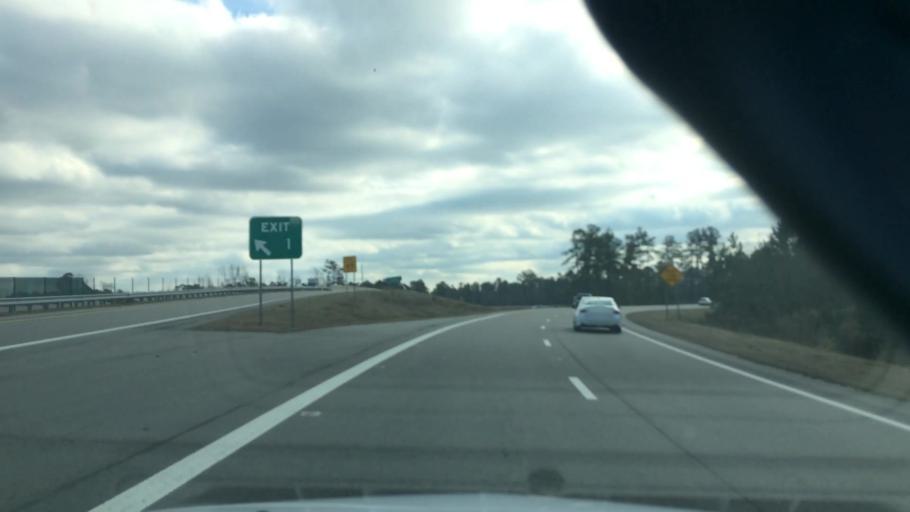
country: US
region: North Carolina
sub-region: Brunswick County
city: Leland
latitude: 34.1928
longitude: -78.0796
